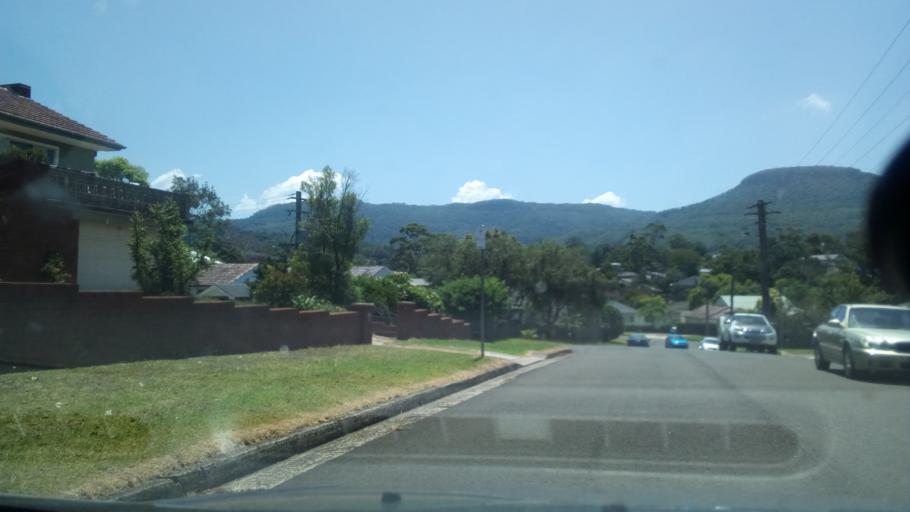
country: AU
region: New South Wales
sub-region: Wollongong
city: West Wollongong
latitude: -34.4290
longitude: 150.8589
